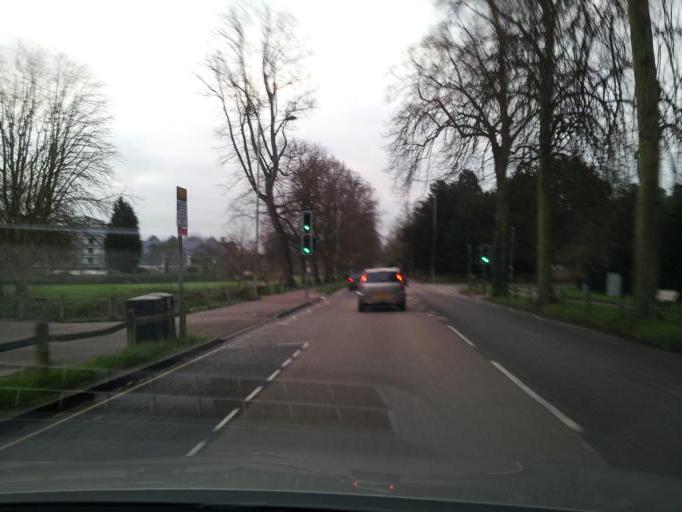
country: GB
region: England
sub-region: Cambridgeshire
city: Cambridge
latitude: 52.2036
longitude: 0.1119
